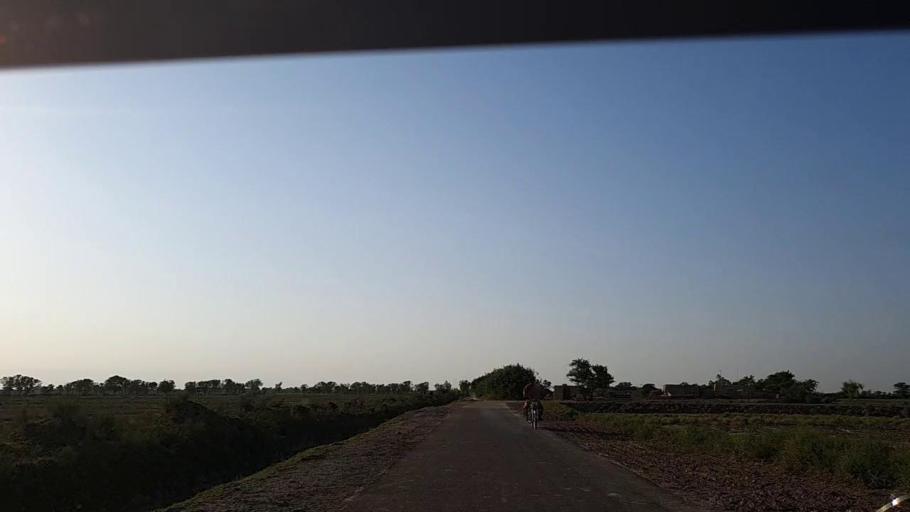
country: PK
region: Sindh
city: Johi
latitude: 26.7432
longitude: 67.5976
